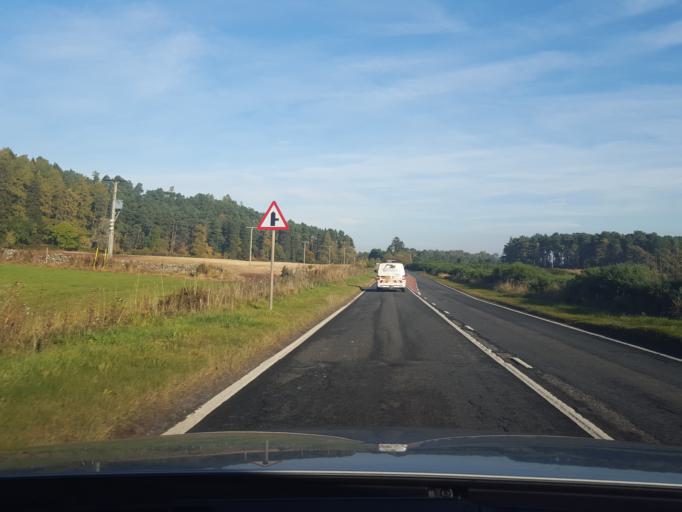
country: GB
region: Scotland
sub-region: Highland
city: Inverness
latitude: 57.4498
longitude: -4.2840
